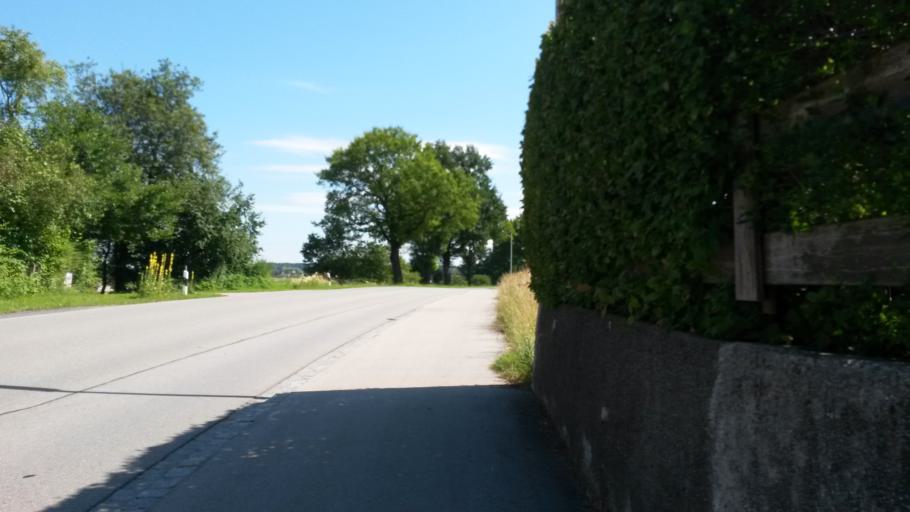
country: DE
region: Bavaria
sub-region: Upper Bavaria
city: Grabenstatt
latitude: 47.8348
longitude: 12.5314
